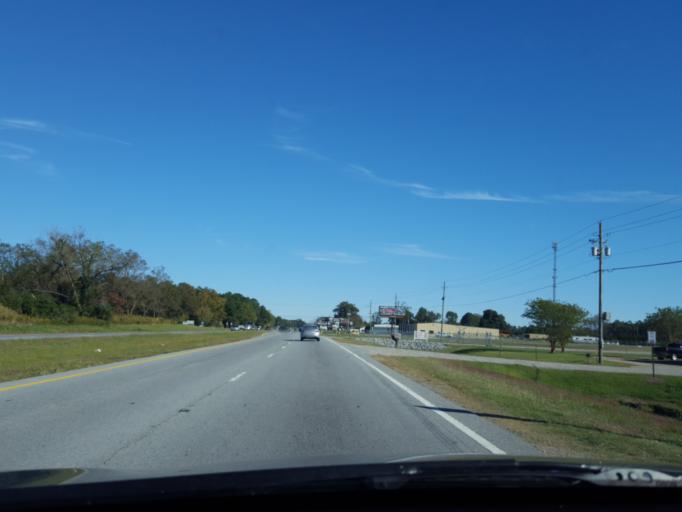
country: US
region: North Carolina
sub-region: Beaufort County
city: Washington
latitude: 35.6042
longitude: -77.1371
